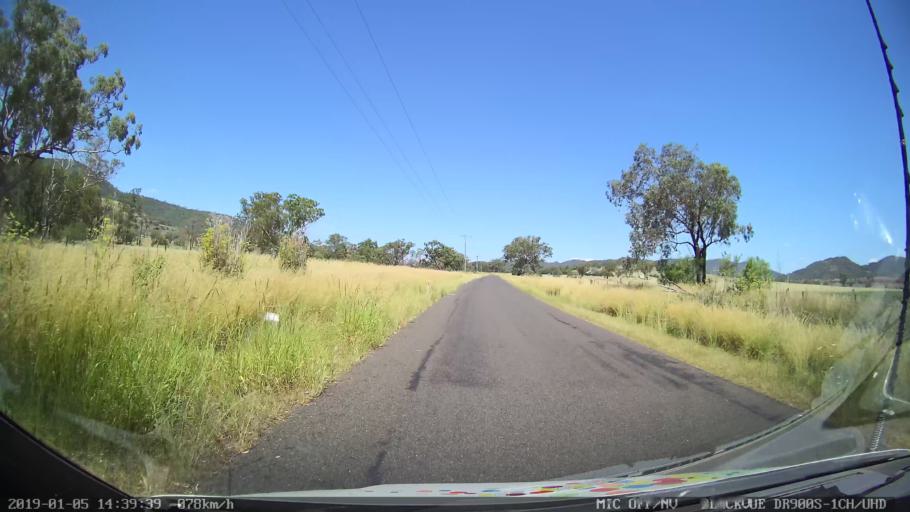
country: AU
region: New South Wales
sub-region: Tamworth Municipality
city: Phillip
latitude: -31.2552
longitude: 150.7031
